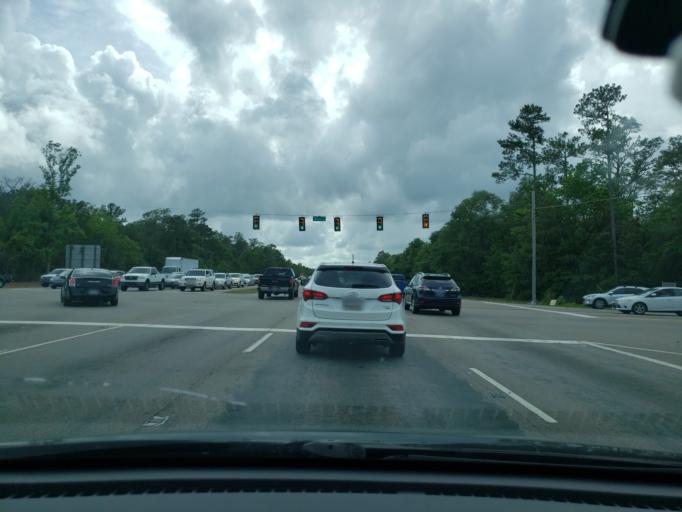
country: US
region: North Carolina
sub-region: New Hanover County
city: Kings Grant
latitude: 34.2542
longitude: -77.8891
